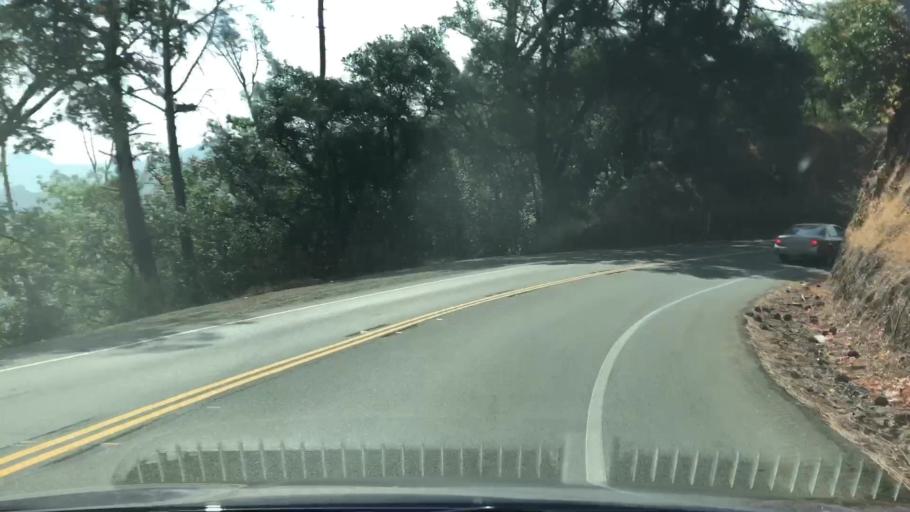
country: US
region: California
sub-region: Napa County
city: Calistoga
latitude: 38.6109
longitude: -122.5942
